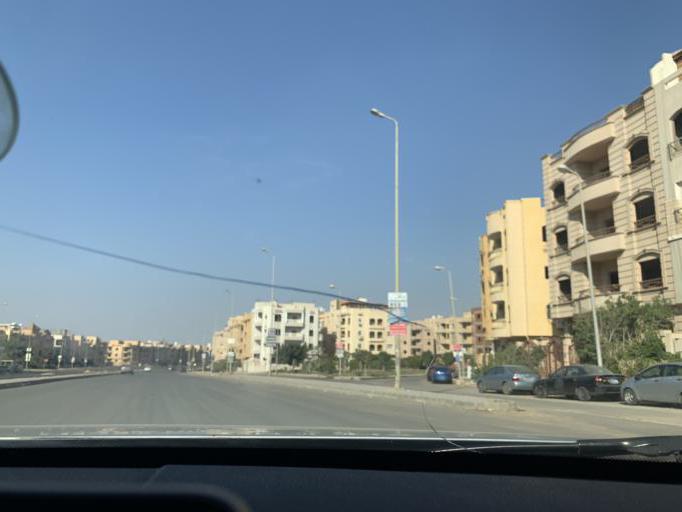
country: EG
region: Muhafazat al Qalyubiyah
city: Al Khankah
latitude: 30.0009
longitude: 31.4805
